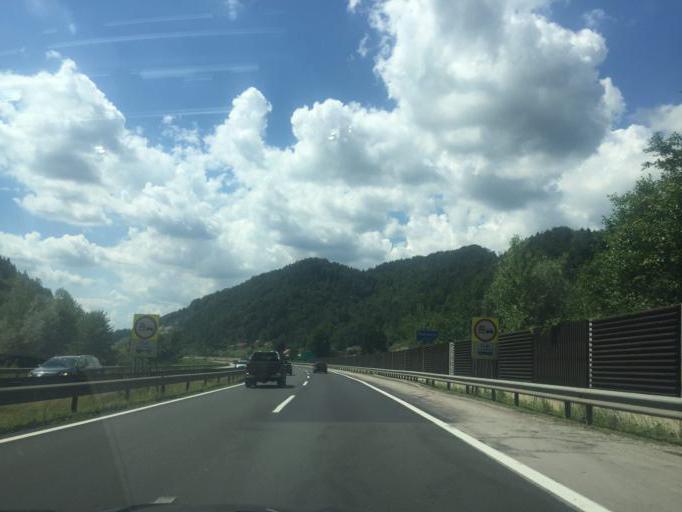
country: SI
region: Moravce
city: Moravce
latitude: 46.1690
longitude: 14.7365
